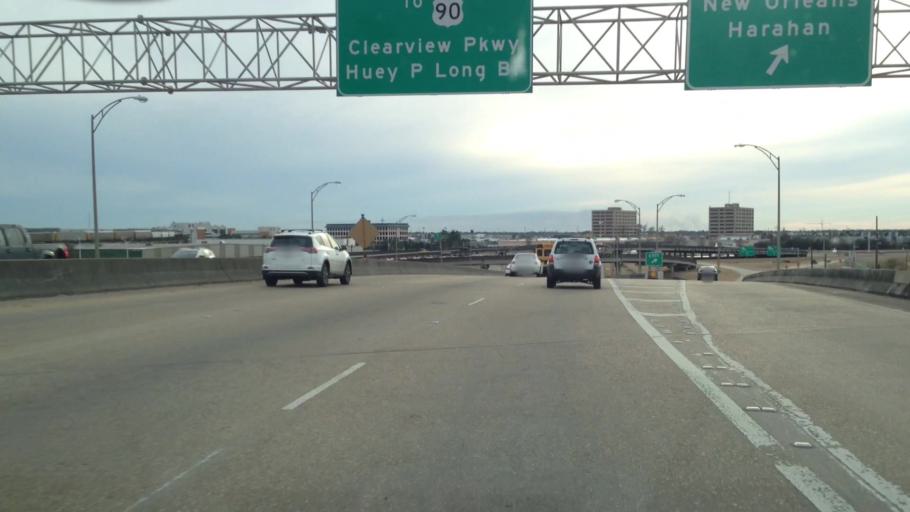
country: US
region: Louisiana
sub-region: Jefferson Parish
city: Metairie Terrace
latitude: 29.9719
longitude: -90.1784
